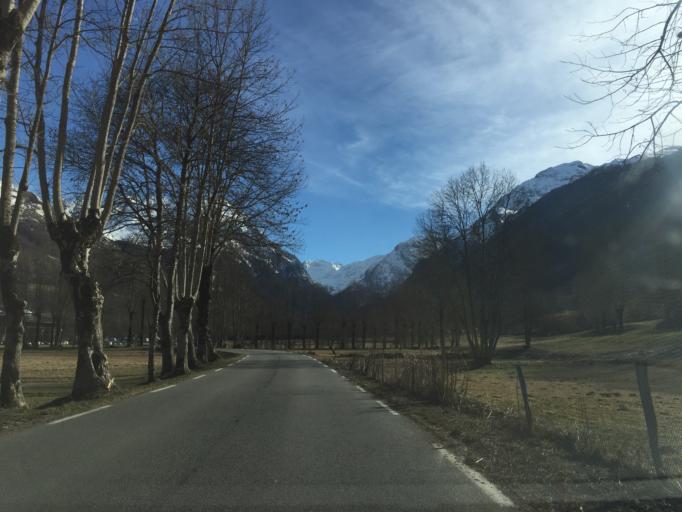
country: FR
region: Midi-Pyrenees
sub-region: Departement des Hautes-Pyrenees
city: Saint-Lary-Soulan
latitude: 42.8008
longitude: 0.4049
